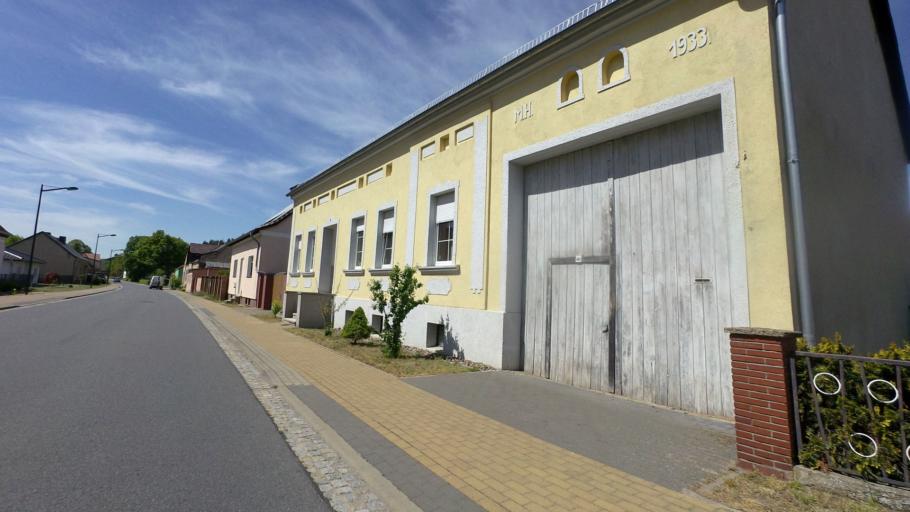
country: DE
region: Brandenburg
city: Sperenberg
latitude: 52.0840
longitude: 13.4115
